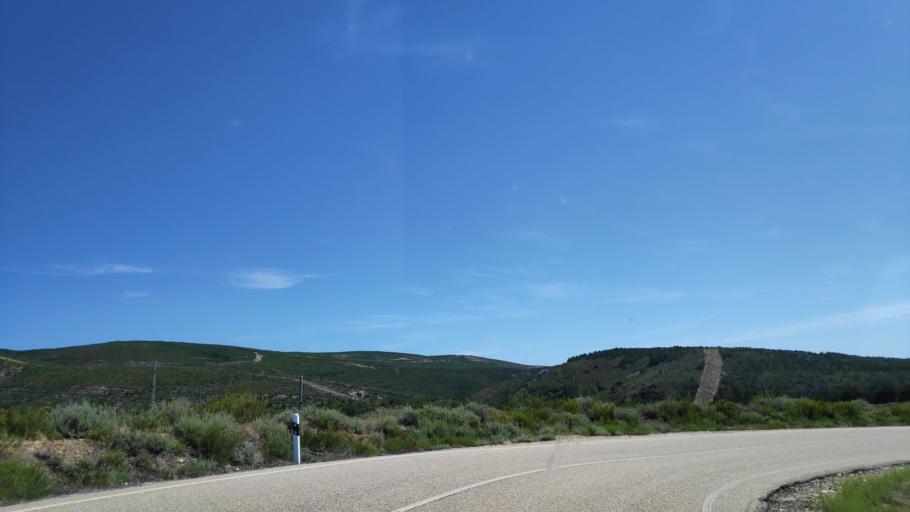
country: ES
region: Castille and Leon
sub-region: Provincia de Zamora
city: Requejo
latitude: 41.9987
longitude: -6.6927
